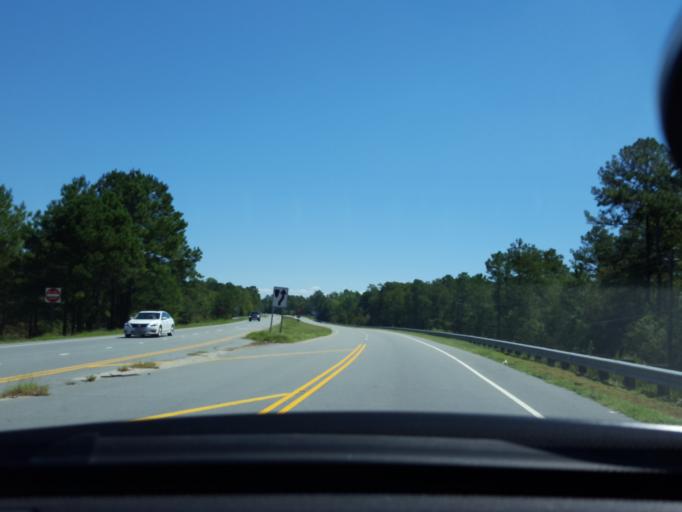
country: US
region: North Carolina
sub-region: Bladen County
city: Elizabethtown
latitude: 34.6471
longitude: -78.5605
